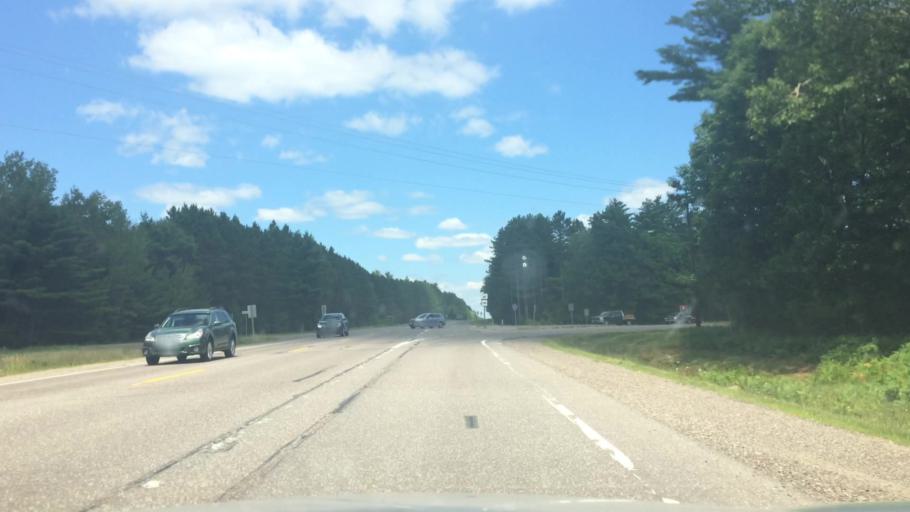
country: US
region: Wisconsin
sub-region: Vilas County
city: Lac du Flambeau
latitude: 45.9816
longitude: -89.6987
